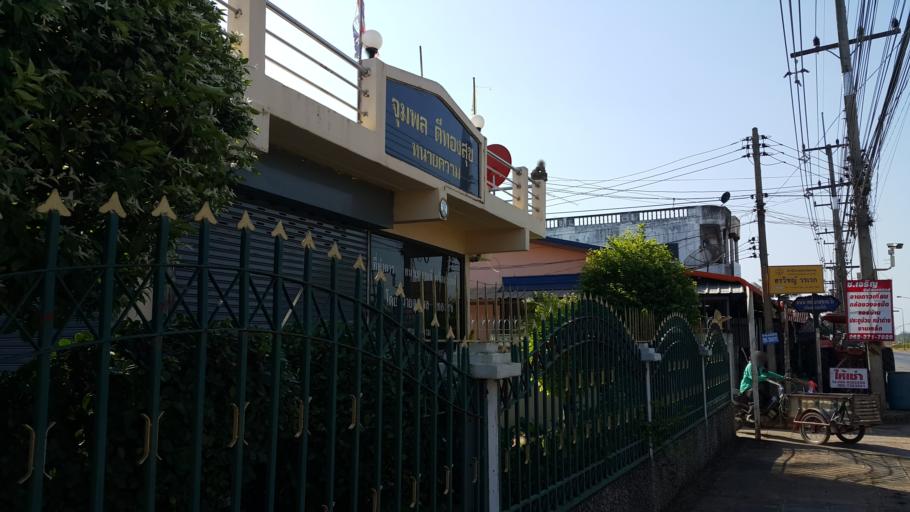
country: TH
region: Sa Kaeo
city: Sa Kaeo
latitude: 13.7850
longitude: 102.1617
